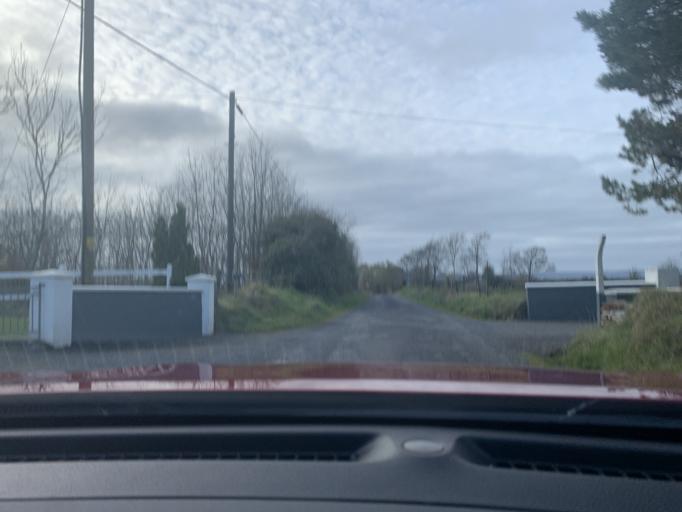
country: IE
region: Connaught
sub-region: Roscommon
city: Ballaghaderreen
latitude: 53.9710
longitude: -8.6213
